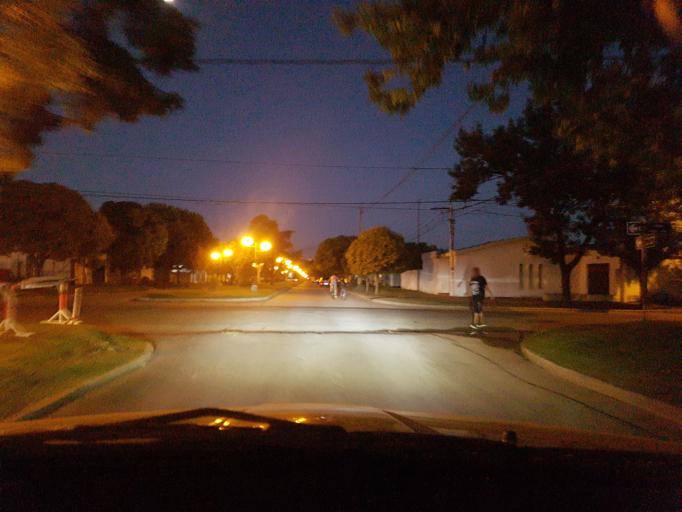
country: AR
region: Cordoba
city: Las Perdices
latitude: -32.7573
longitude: -63.7829
